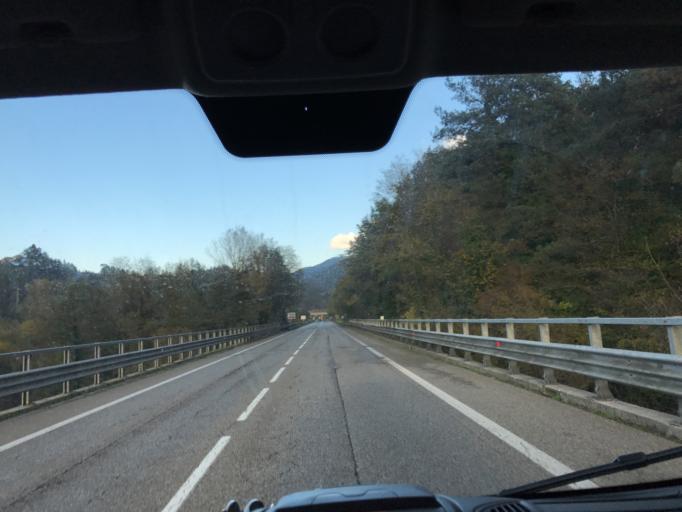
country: IT
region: The Marches
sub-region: Provincia di Ascoli Piceno
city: Marsia
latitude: 42.8044
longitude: 13.4880
